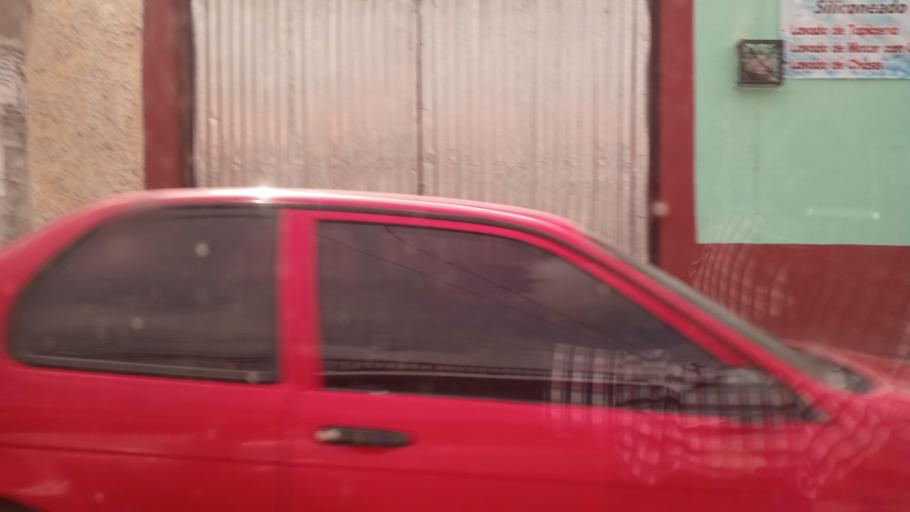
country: GT
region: Quetzaltenango
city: Quetzaltenango
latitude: 14.8302
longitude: -91.5270
